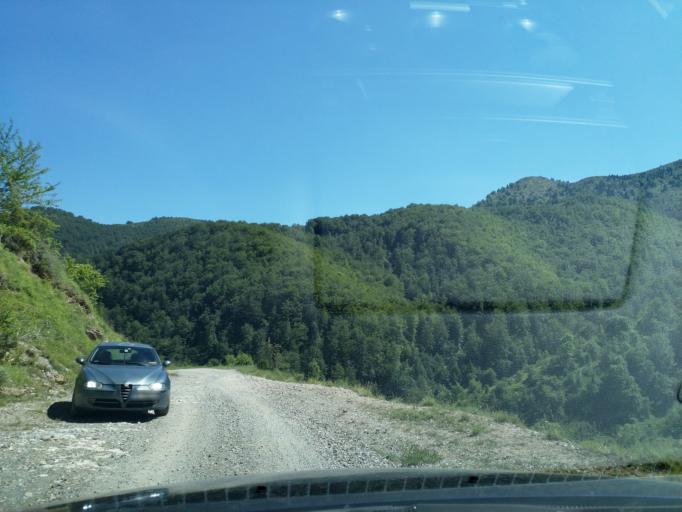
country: XK
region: Mitrovica
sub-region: Komuna e Leposaviqit
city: Leposaviq
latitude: 43.2660
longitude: 20.8607
